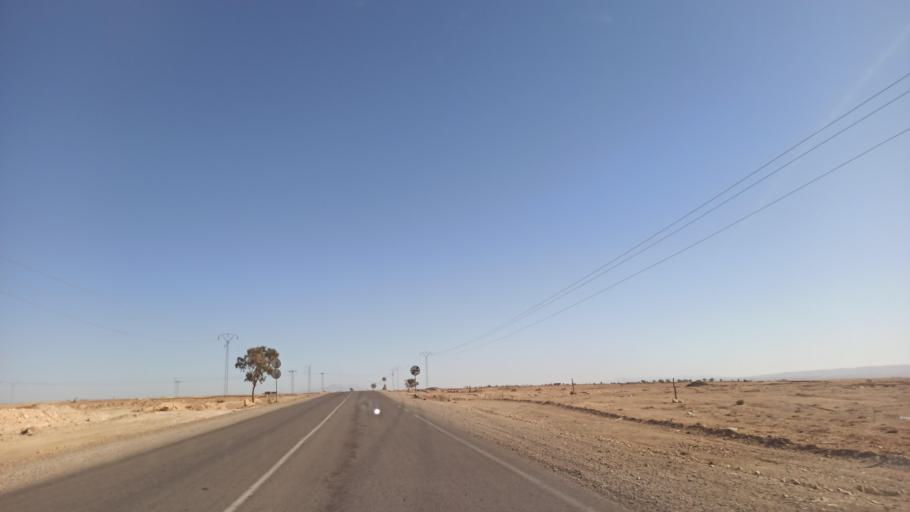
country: TN
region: Gafsa
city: Al Metlaoui
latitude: 34.3119
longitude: 8.4759
